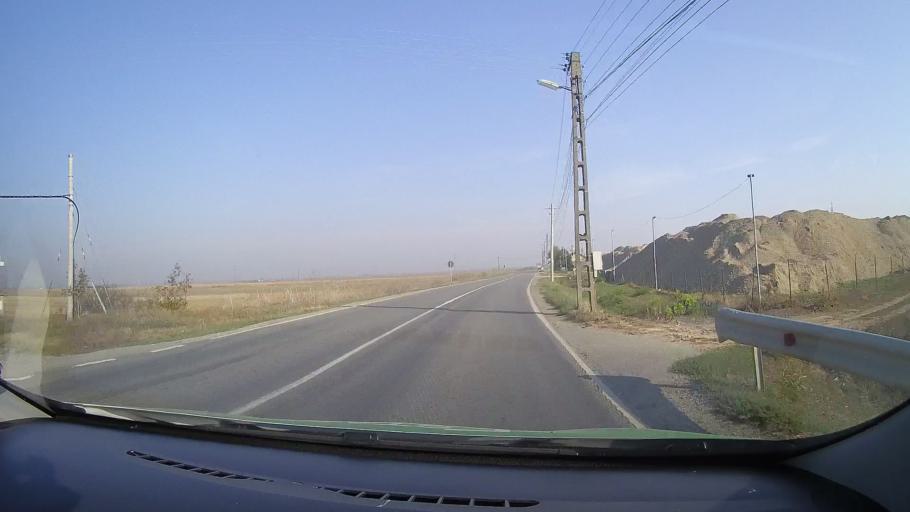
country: RO
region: Arad
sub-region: Comuna Pilu
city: Pilu
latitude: 46.5831
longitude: 21.3438
